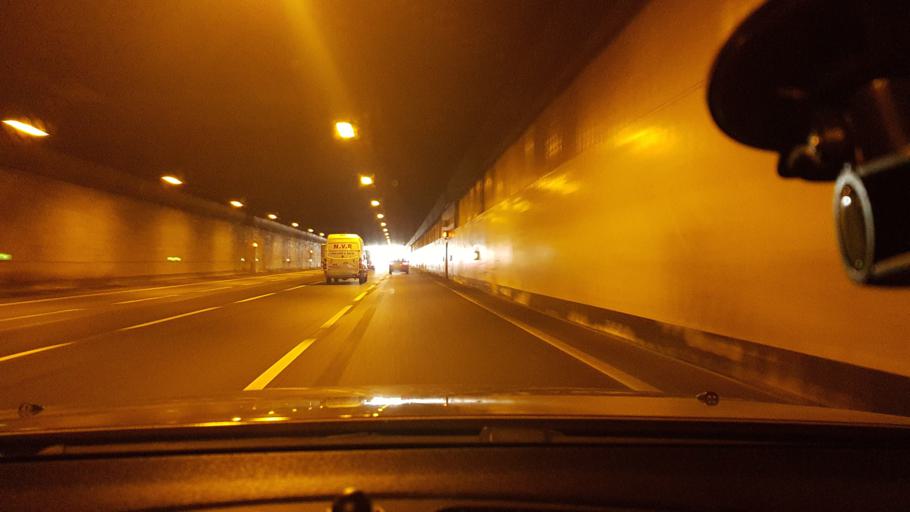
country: GB
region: England
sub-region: Hertfordshire
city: Waltham Cross
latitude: 51.6827
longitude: -0.0373
